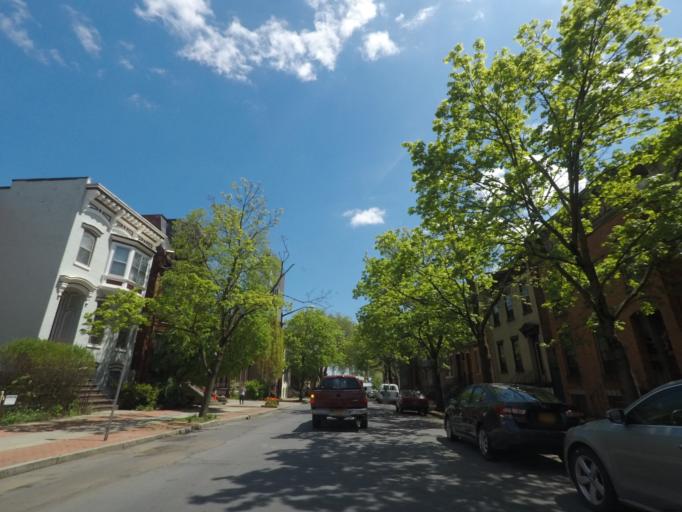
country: US
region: New York
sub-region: Albany County
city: Albany
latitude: 42.6508
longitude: -73.7647
